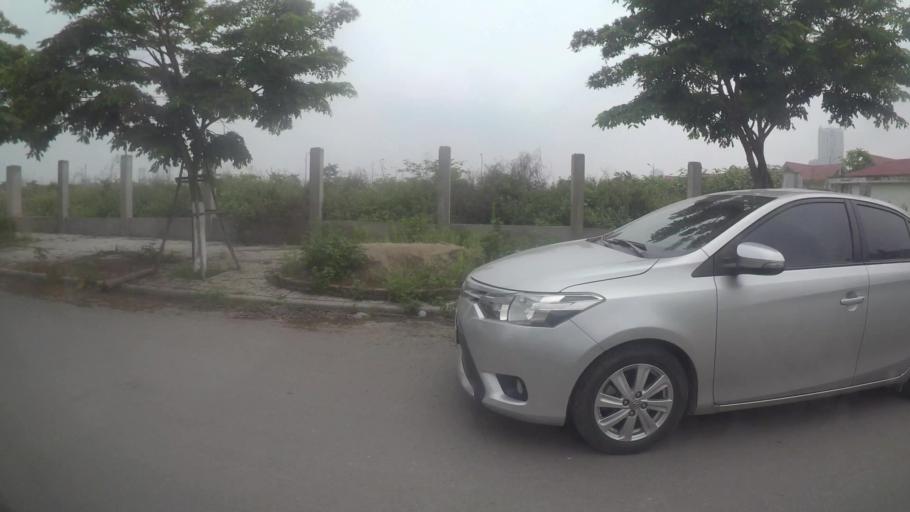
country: VN
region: Ha Noi
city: Ha Dong
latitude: 20.9770
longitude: 105.7532
